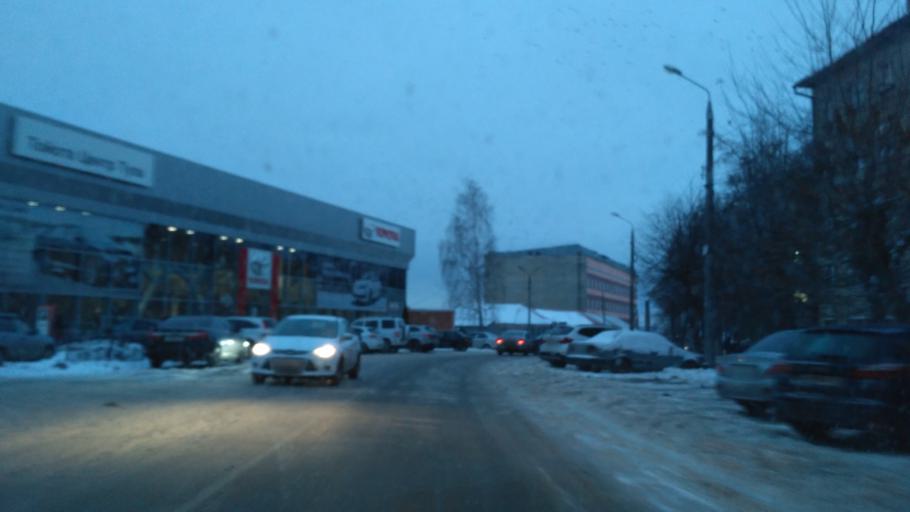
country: RU
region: Tula
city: Mendeleyevskiy
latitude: 54.1637
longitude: 37.5817
